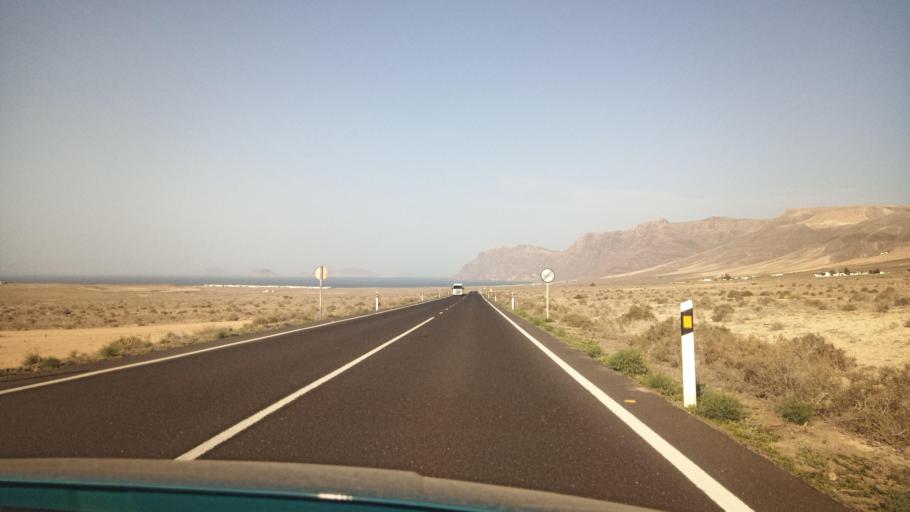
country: ES
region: Canary Islands
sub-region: Provincia de Las Palmas
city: Teguise
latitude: 29.0785
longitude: -13.5763
